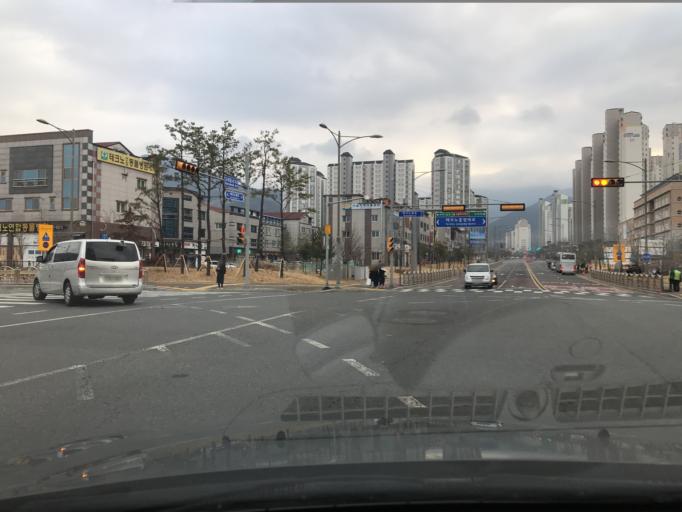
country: KR
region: Daegu
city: Hwawon
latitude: 35.6968
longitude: 128.4575
